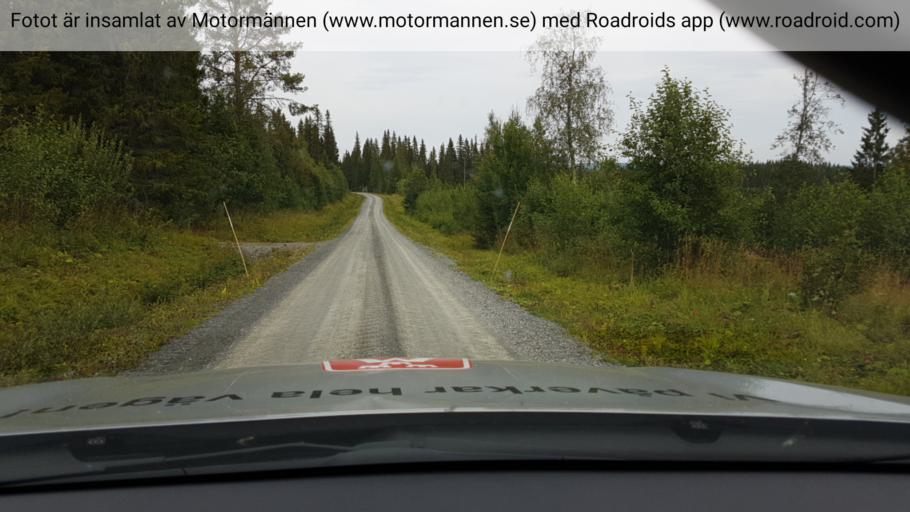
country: SE
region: Jaemtland
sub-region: Krokoms Kommun
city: Valla
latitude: 63.5771
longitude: 13.9417
